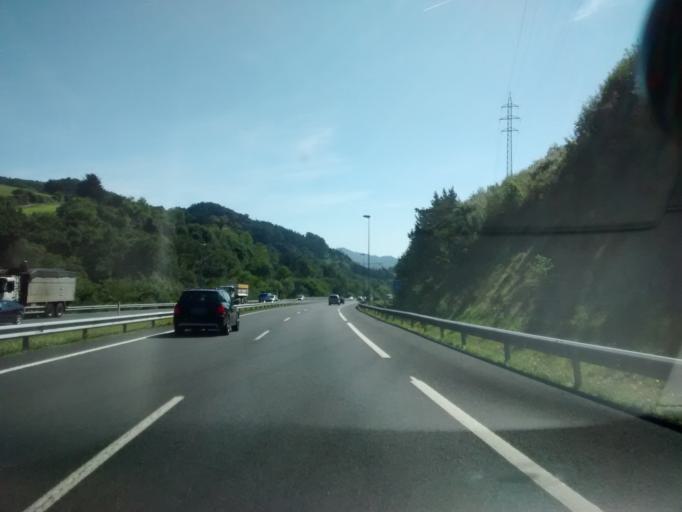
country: ES
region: Basque Country
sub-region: Provincia de Guipuzcoa
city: Getaria
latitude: 43.2812
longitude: -2.2041
